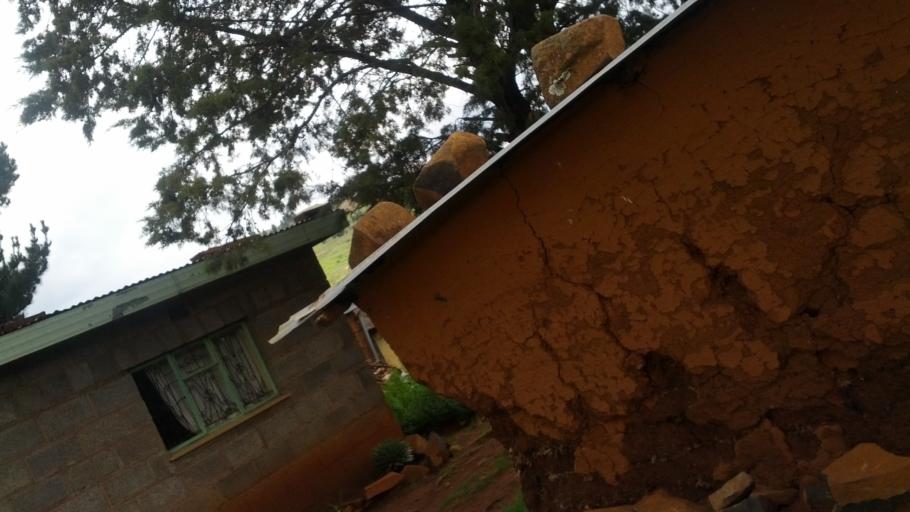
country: LS
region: Maseru
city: Nako
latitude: -29.5892
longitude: 27.7566
